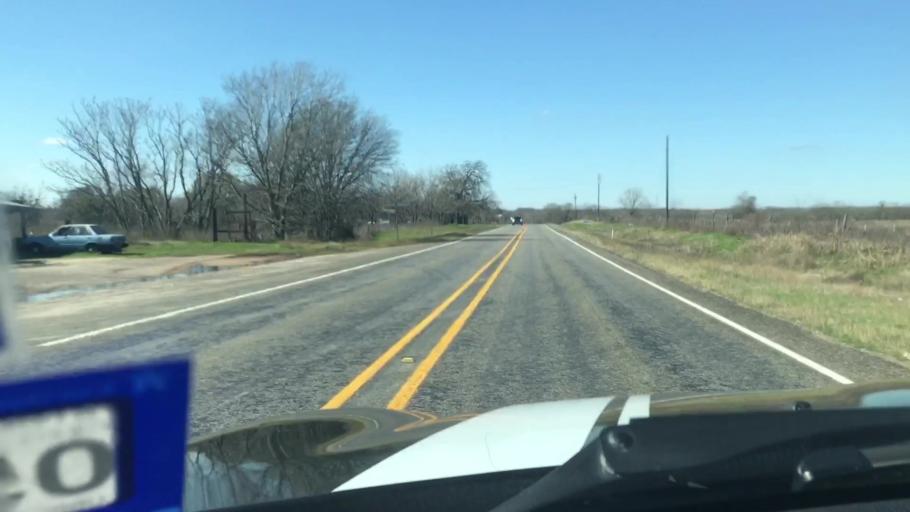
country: US
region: Texas
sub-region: Robertson County
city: Calvert
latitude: 30.8847
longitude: -96.7540
